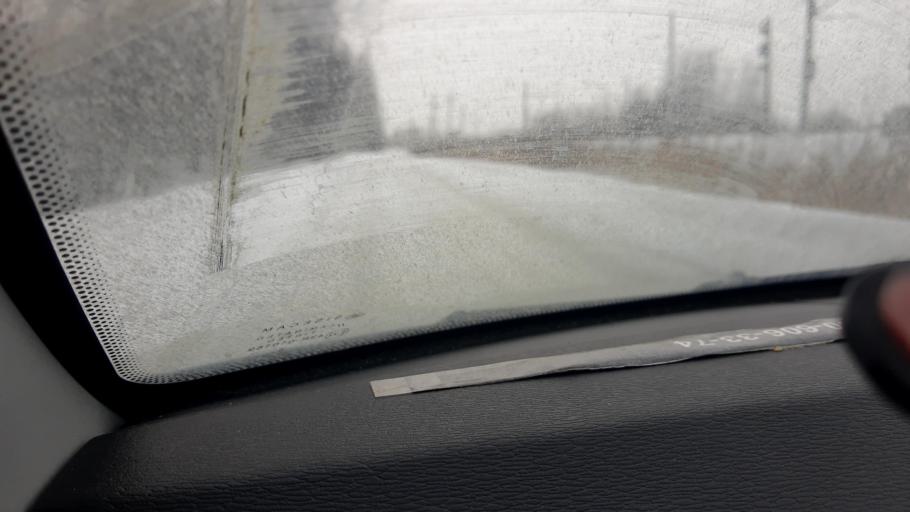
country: RU
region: Nizjnij Novgorod
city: Sitniki
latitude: 56.5229
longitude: 44.0518
